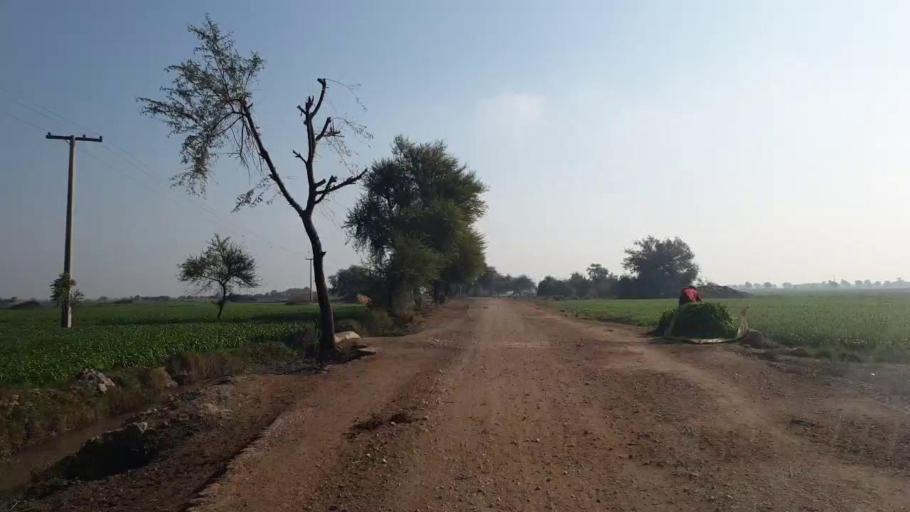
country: PK
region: Sindh
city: Shahdadpur
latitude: 26.0036
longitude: 68.6421
